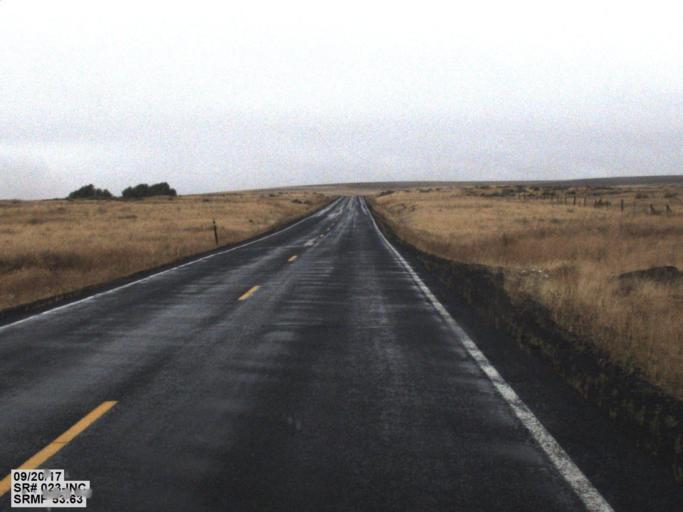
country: US
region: Washington
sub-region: Lincoln County
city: Davenport
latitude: 47.3708
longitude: -118.1154
